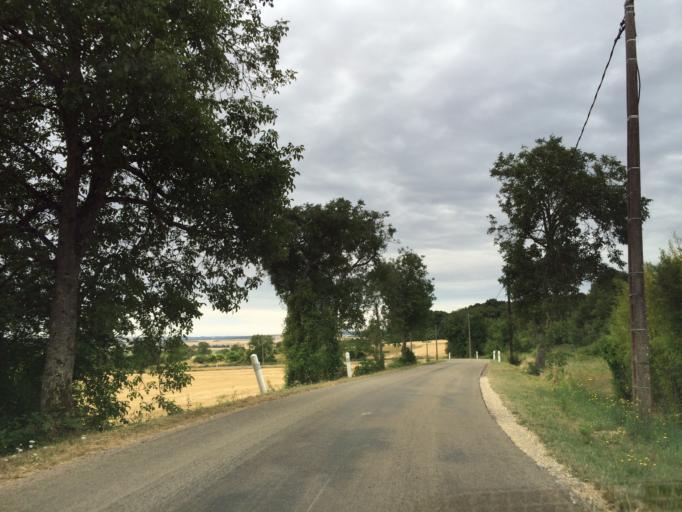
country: FR
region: Bourgogne
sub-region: Departement de l'Yonne
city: Aillant-sur-Tholon
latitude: 47.8739
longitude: 3.3141
